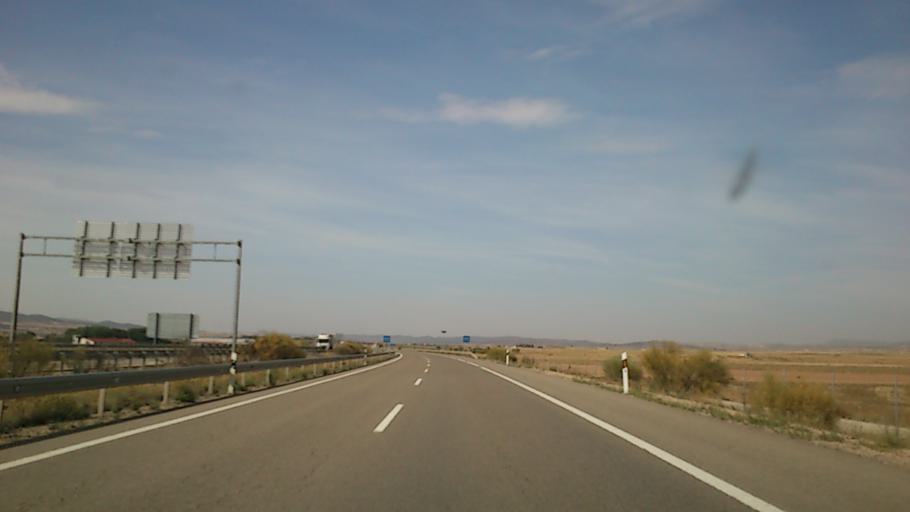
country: ES
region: Aragon
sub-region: Provincia de Teruel
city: Caminreal
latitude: 40.8431
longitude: -1.3093
